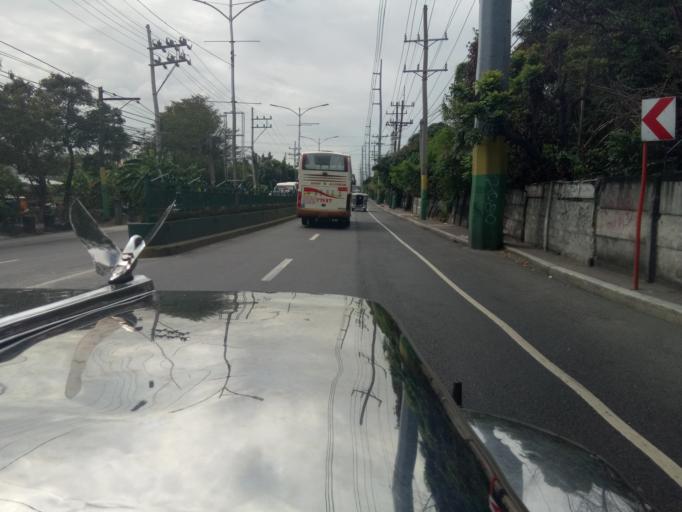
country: PH
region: Calabarzon
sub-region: Province of Cavite
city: Dasmarinas
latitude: 14.3080
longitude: 120.9521
